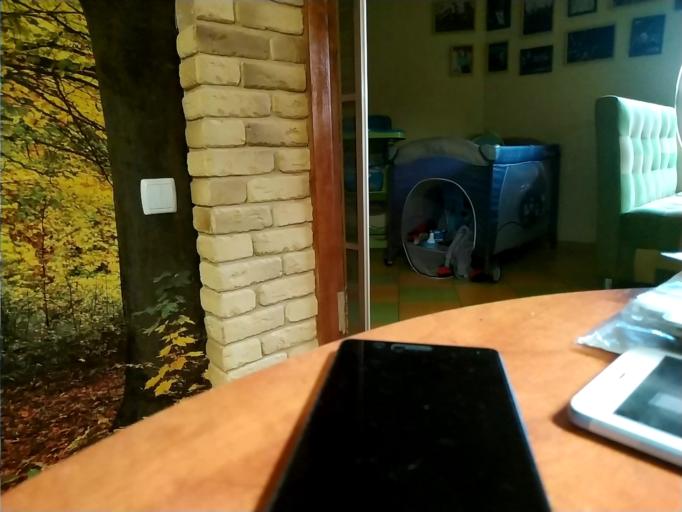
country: RU
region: Kaluga
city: Khvastovichi
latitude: 53.6088
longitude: 35.4660
